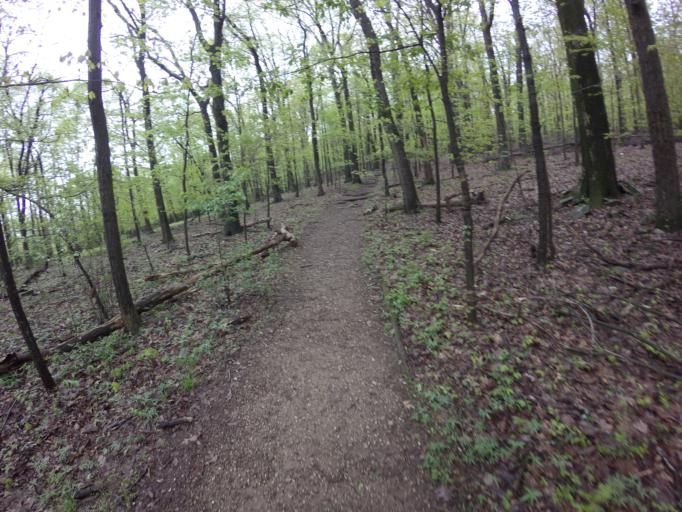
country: US
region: Maryland
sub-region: Washington County
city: Boonsboro
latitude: 39.5268
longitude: -77.6130
